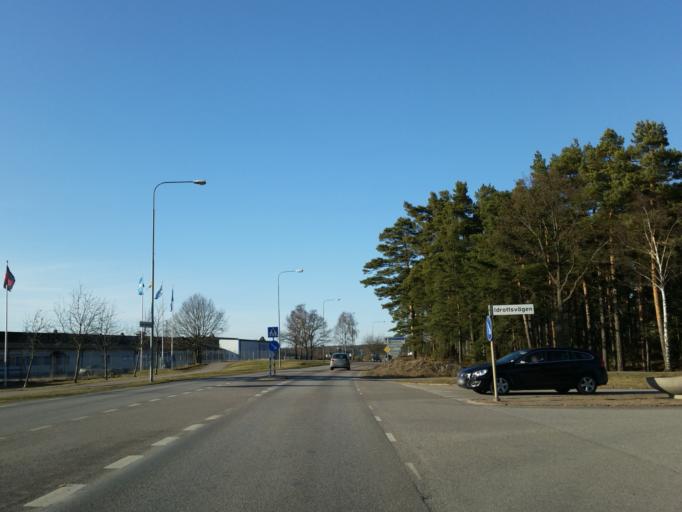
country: SE
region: Kalmar
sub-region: Oskarshamns Kommun
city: Oskarshamn
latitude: 57.2599
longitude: 16.4310
